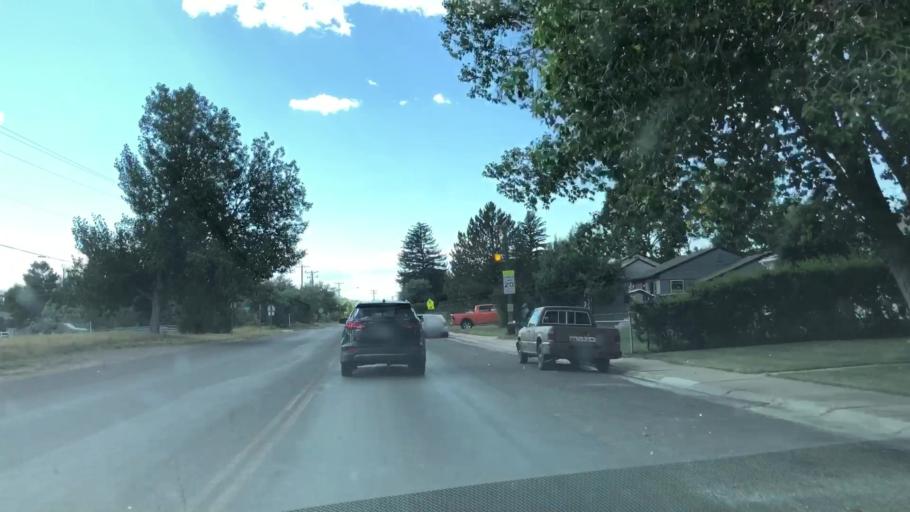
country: US
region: Wyoming
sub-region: Albany County
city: Laramie
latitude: 41.3029
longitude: -105.5801
